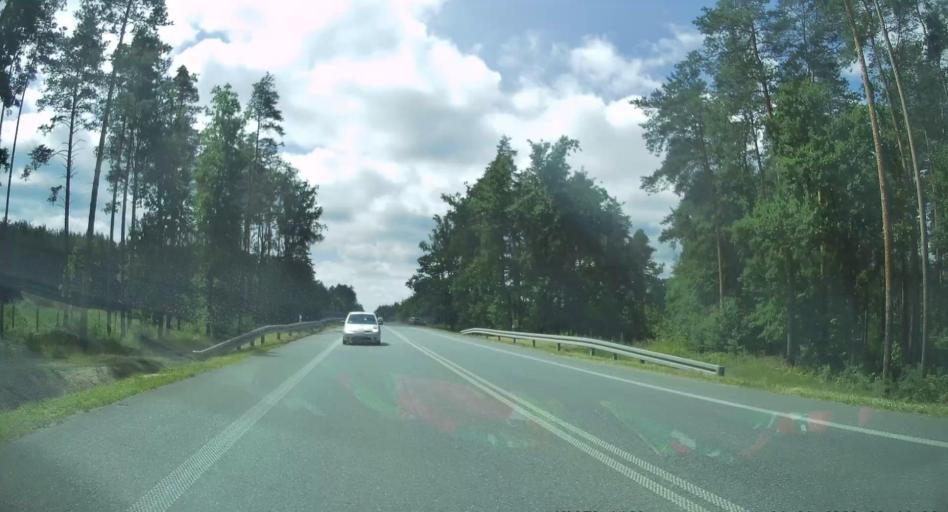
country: PL
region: Subcarpathian Voivodeship
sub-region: Powiat mielecki
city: Mielec
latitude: 50.3118
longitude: 21.5033
